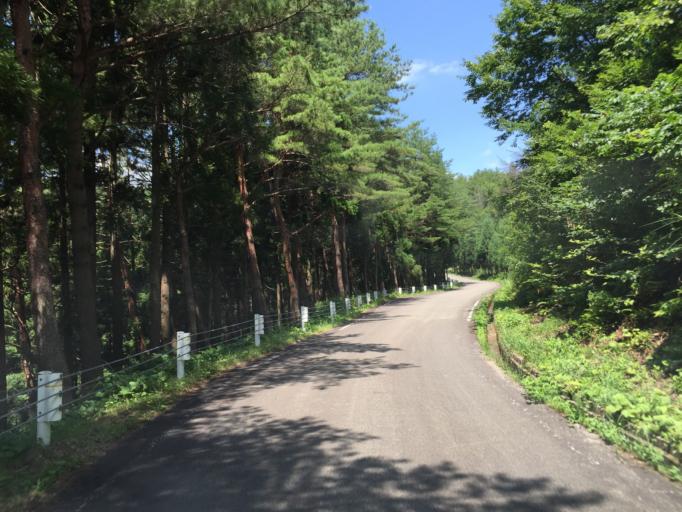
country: JP
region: Fukushima
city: Inawashiro
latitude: 37.4710
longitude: 140.0421
